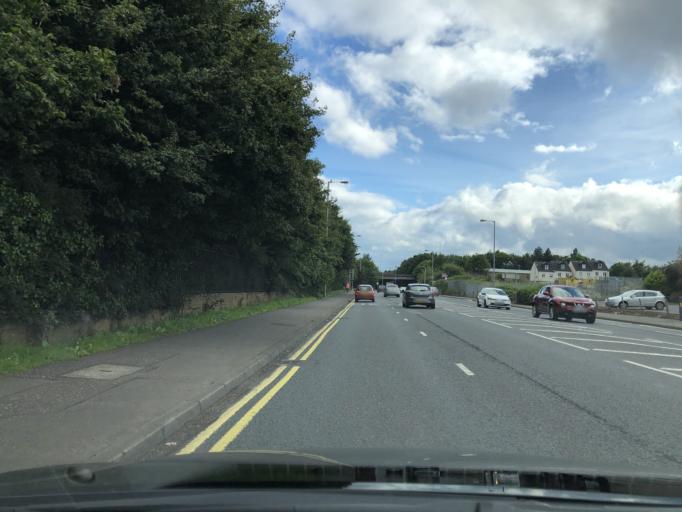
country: GB
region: Northern Ireland
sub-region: Newtownabbey District
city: Newtownabbey
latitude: 54.6510
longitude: -5.9181
